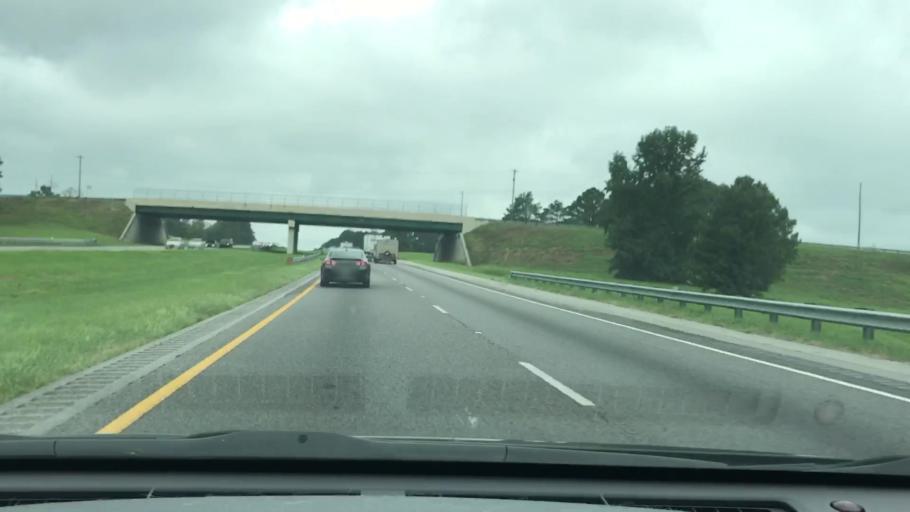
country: US
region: Georgia
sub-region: Walton County
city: Social Circle
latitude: 33.6125
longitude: -83.7483
